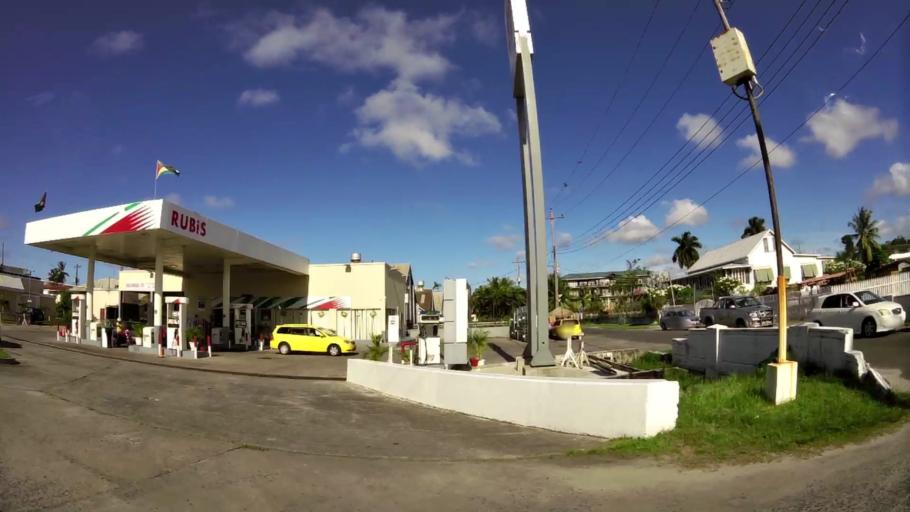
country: GY
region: Demerara-Mahaica
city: Georgetown
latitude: 6.8103
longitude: -58.1472
